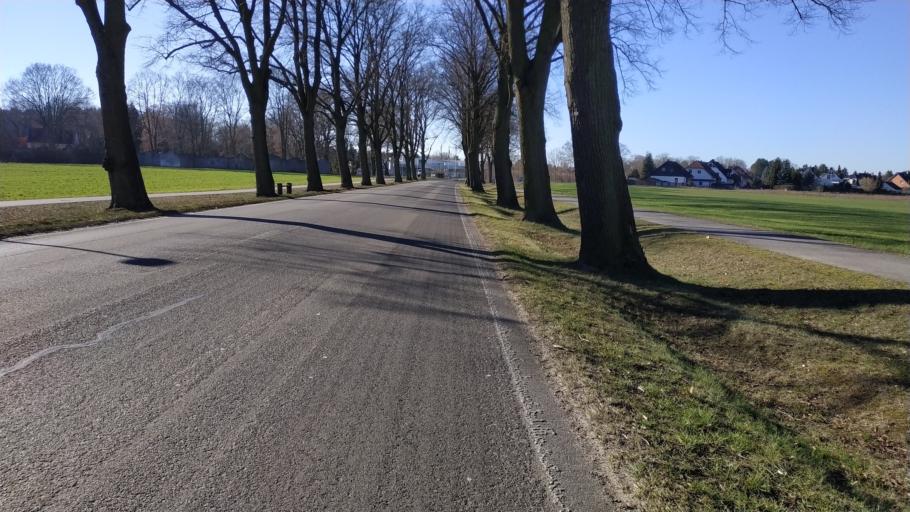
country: DE
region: Brandenburg
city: Petershagen
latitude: 52.5344
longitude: 13.8123
